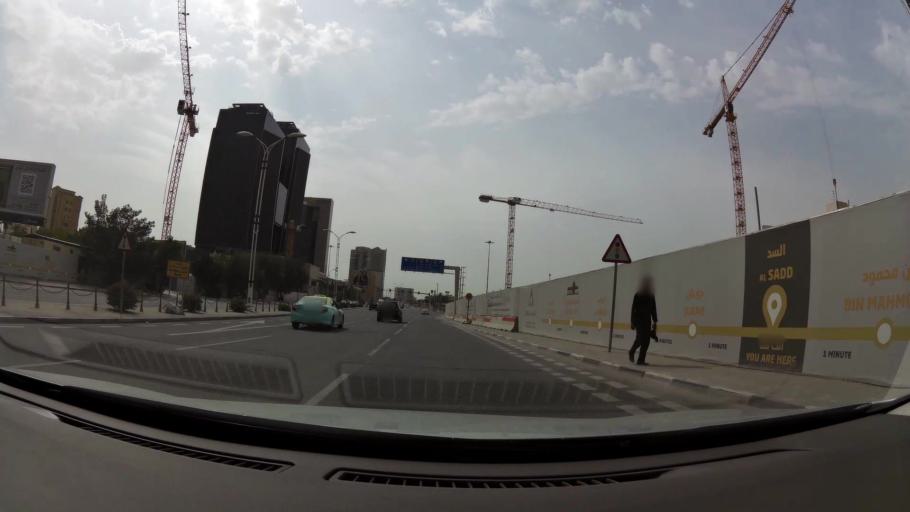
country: QA
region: Baladiyat ad Dawhah
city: Doha
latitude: 25.2830
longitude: 51.5059
